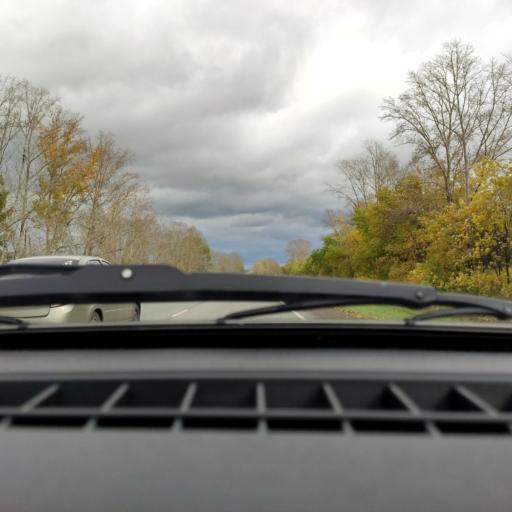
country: RU
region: Bashkortostan
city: Shafranovo
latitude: 54.0140
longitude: 54.8063
